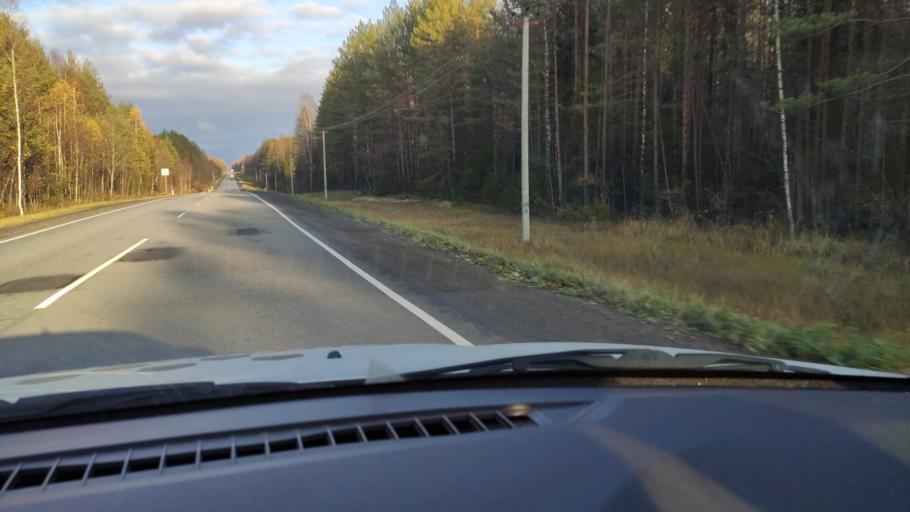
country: RU
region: Kirov
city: Belaya Kholunitsa
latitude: 58.9127
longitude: 51.0719
